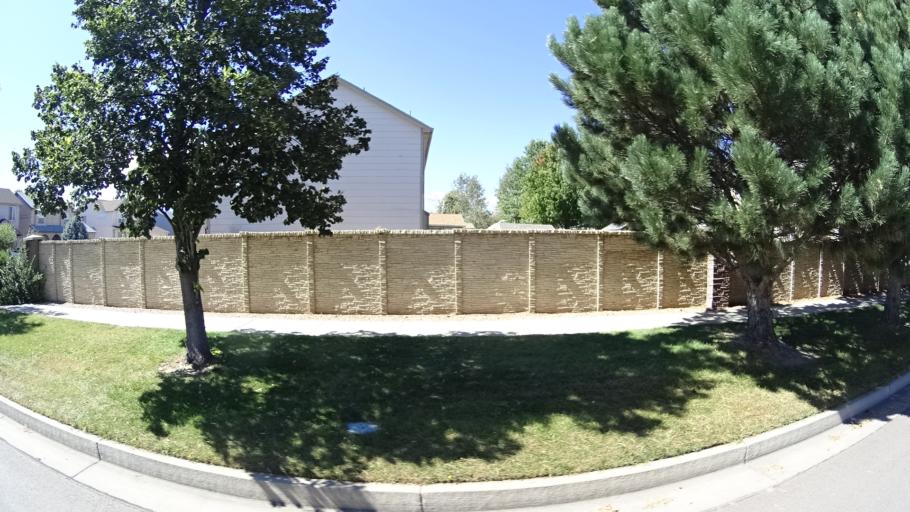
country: US
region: Colorado
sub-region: El Paso County
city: Security-Widefield
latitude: 38.7842
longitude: -104.7294
